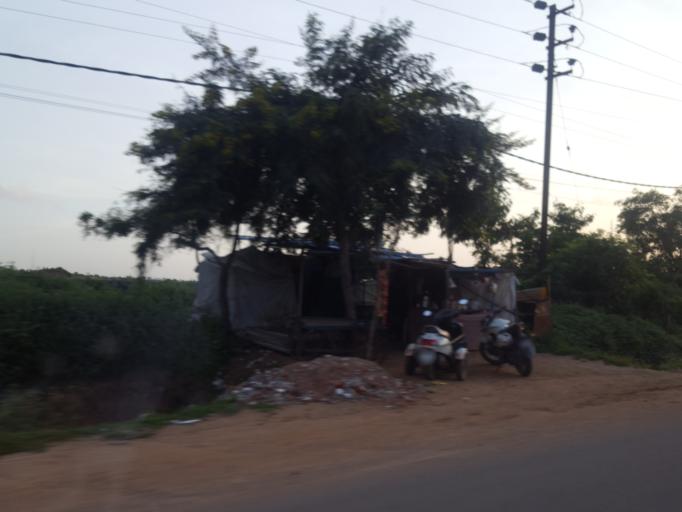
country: IN
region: Telangana
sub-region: Rangareddi
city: Kukatpalli
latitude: 17.5420
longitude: 78.3856
